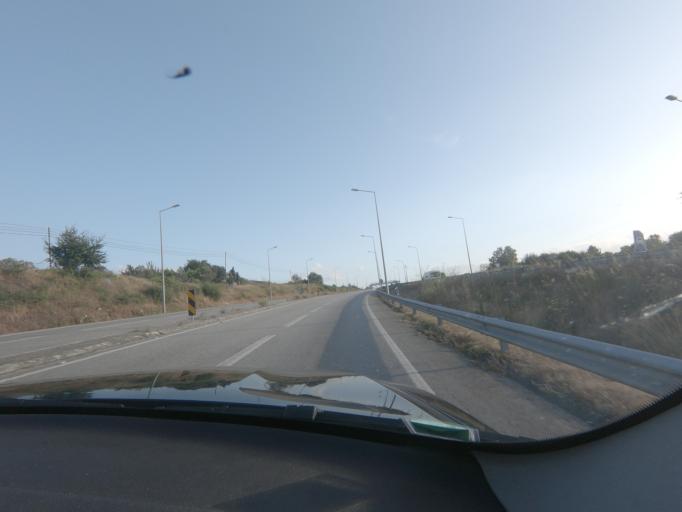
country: PT
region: Viseu
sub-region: Santa Comba Dao
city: Santa Comba Dao
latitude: 40.3799
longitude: -8.1181
